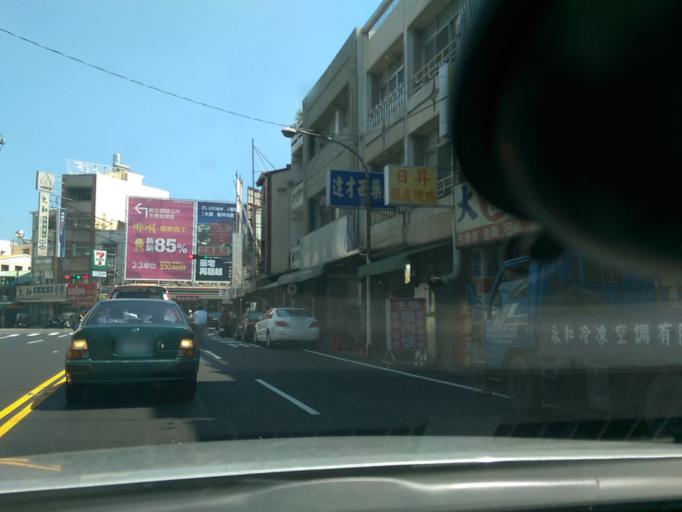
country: TW
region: Taiwan
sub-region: Chiayi
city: Jiayi Shi
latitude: 23.4514
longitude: 120.4603
